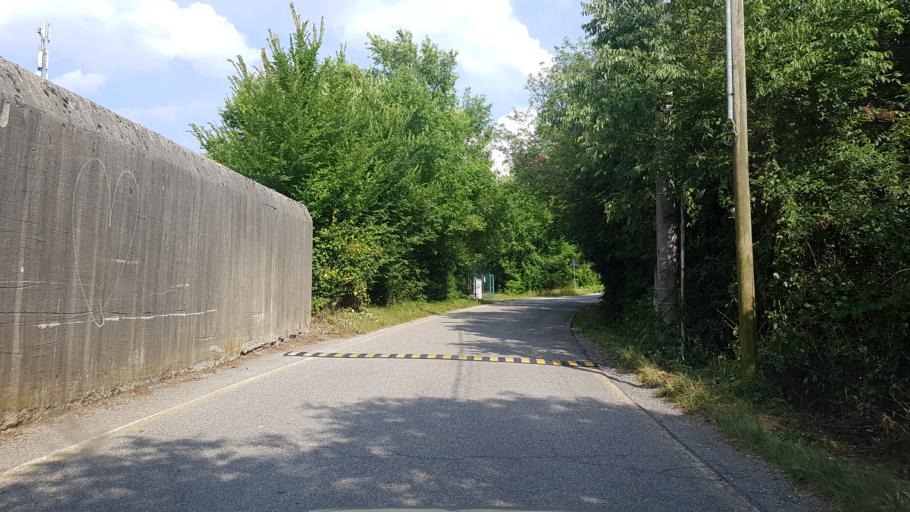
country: IT
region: Friuli Venezia Giulia
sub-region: Provincia di Gorizia
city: Savogna d'Isonzo
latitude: 45.9031
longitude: 13.5751
